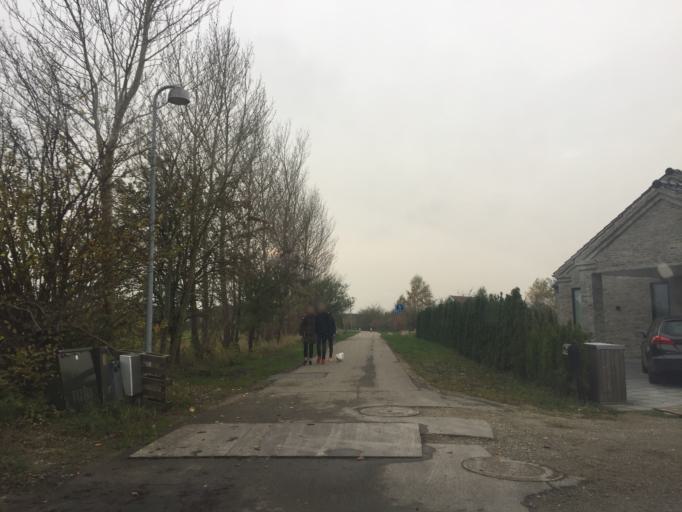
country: DK
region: Capital Region
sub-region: Hoje-Taastrup Kommune
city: Taastrup
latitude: 55.6505
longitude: 12.2532
